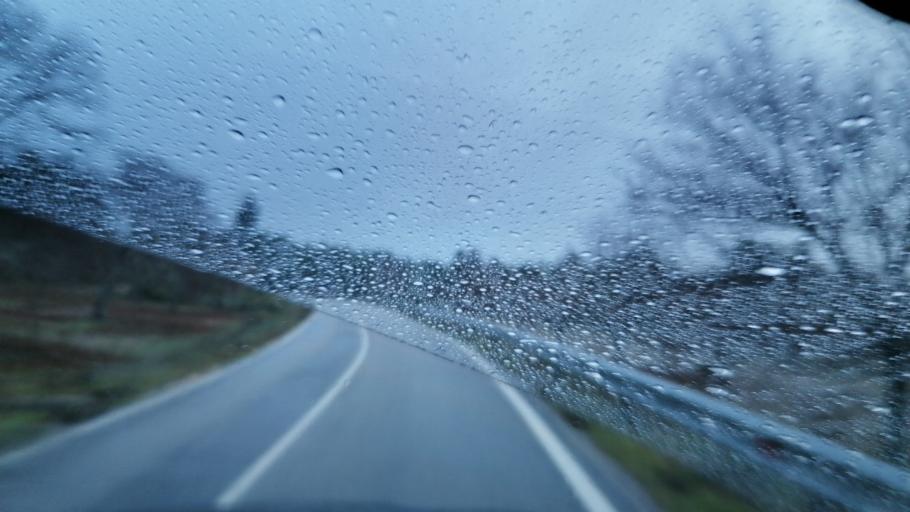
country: PT
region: Vila Real
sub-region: Murca
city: Murca
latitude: 41.4401
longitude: -7.5289
